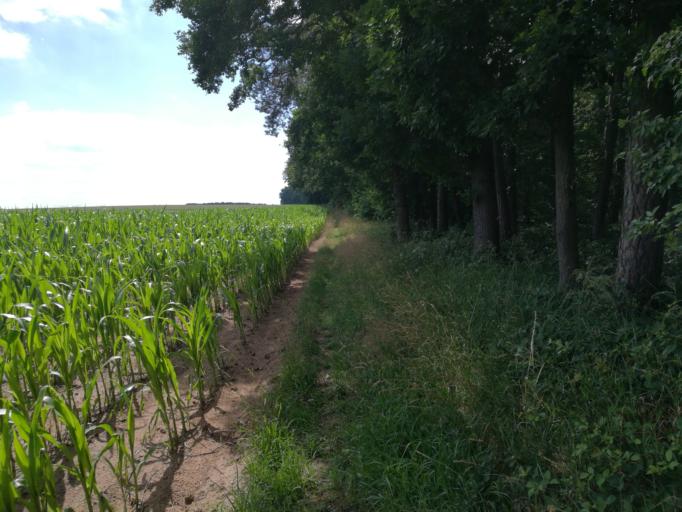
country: DE
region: Bavaria
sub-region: Regierungsbezirk Mittelfranken
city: Seukendorf
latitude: 49.4954
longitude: 10.8919
